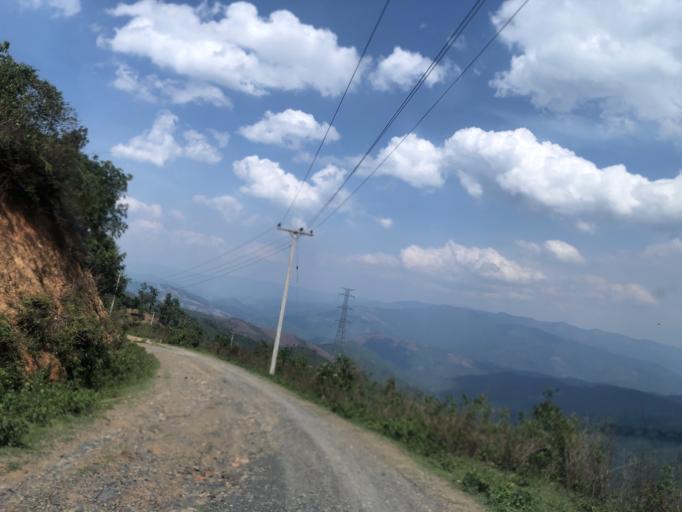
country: LA
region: Phongsali
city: Phongsali
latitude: 21.4112
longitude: 102.2433
